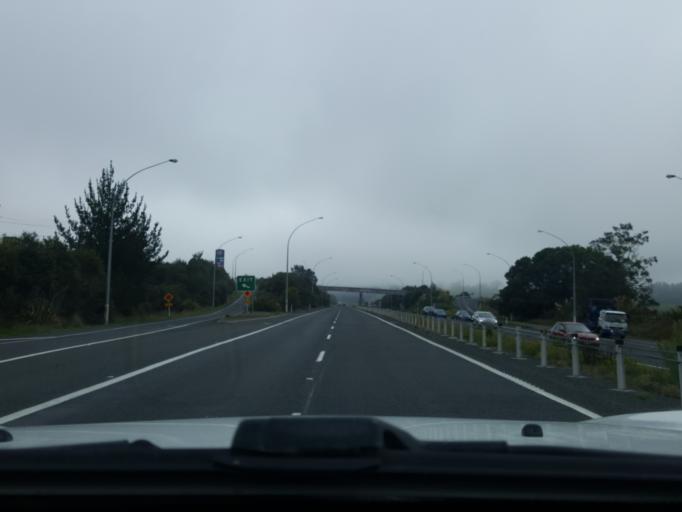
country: NZ
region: Waikato
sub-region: Waikato District
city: Te Kauwhata
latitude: -37.3572
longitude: 175.0848
